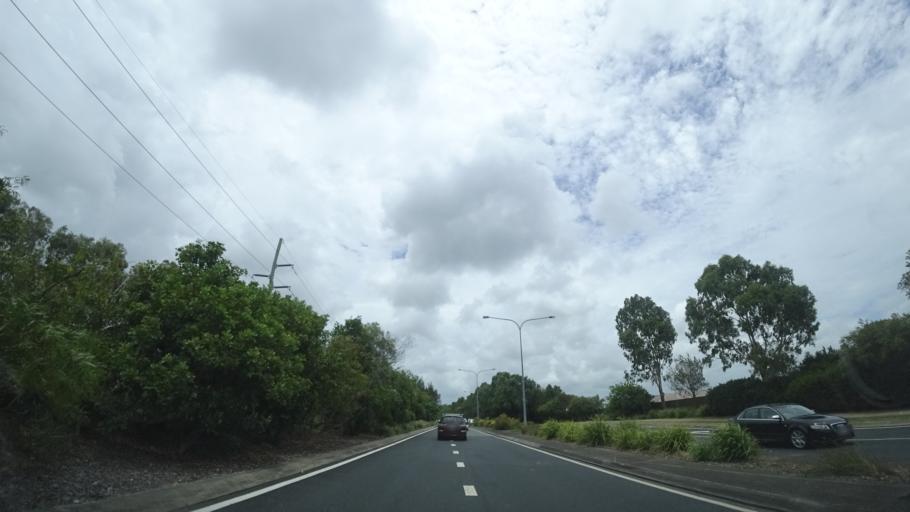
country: AU
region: Queensland
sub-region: Sunshine Coast
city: Mooloolaba
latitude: -26.7145
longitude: 153.0989
